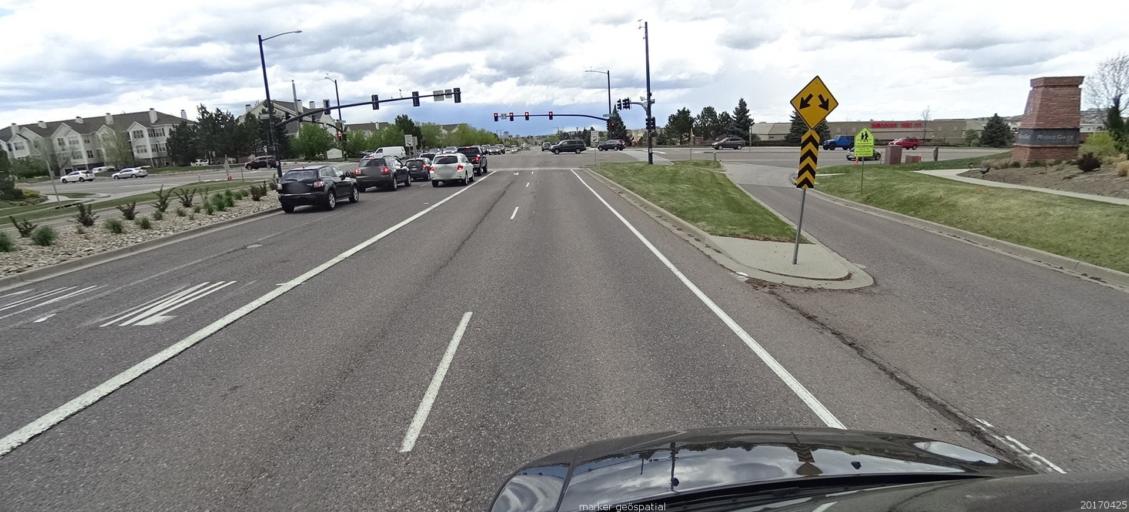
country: US
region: Colorado
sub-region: Douglas County
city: Carriage Club
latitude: 39.5357
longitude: -104.8855
